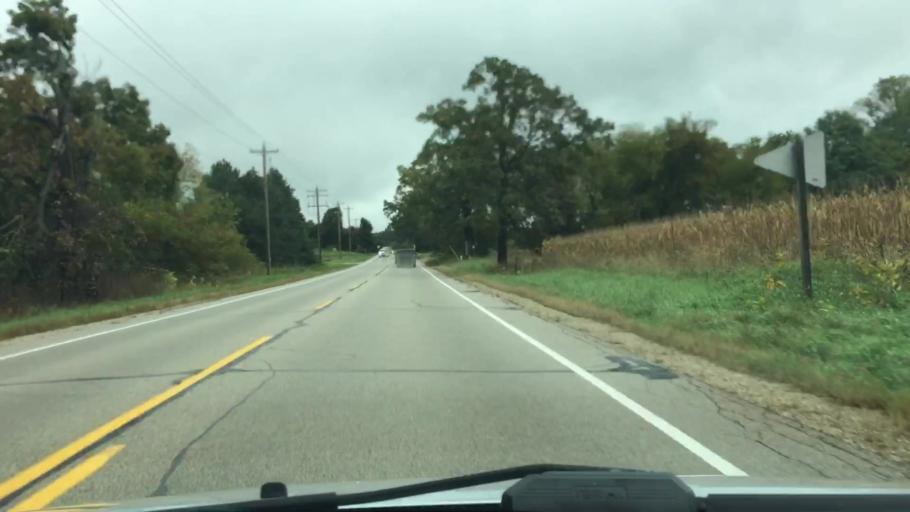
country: US
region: Wisconsin
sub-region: Waukesha County
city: Dousman
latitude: 42.9735
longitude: -88.4710
